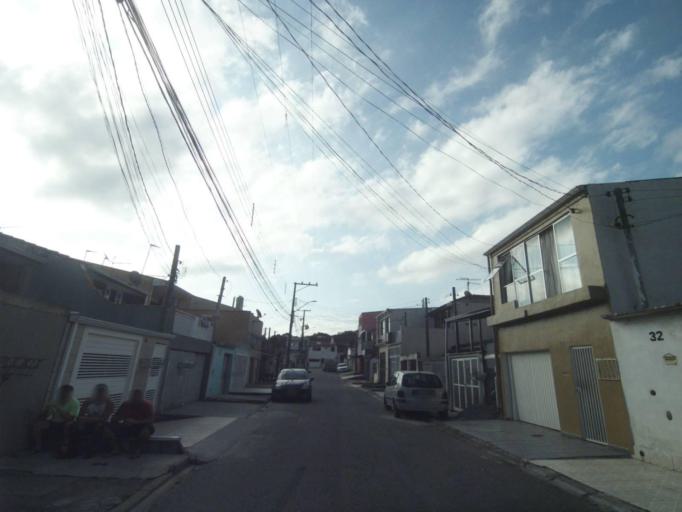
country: BR
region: Parana
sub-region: Araucaria
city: Araucaria
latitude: -25.5343
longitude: -49.3314
